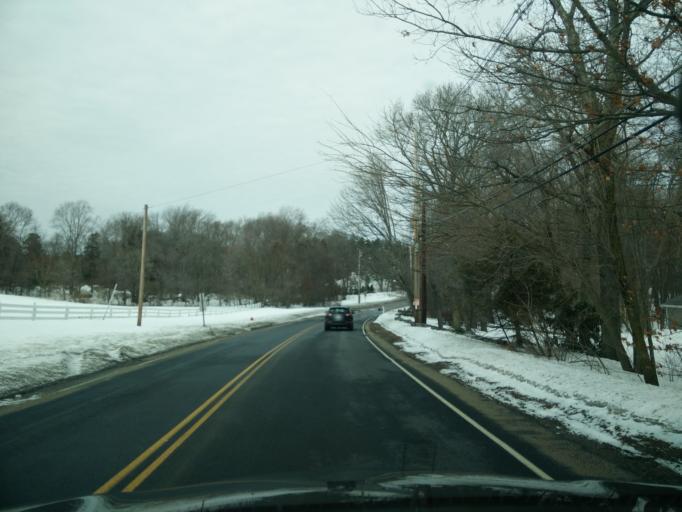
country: US
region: Massachusetts
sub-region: Norfolk County
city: Westwood
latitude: 42.1995
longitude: -71.2499
